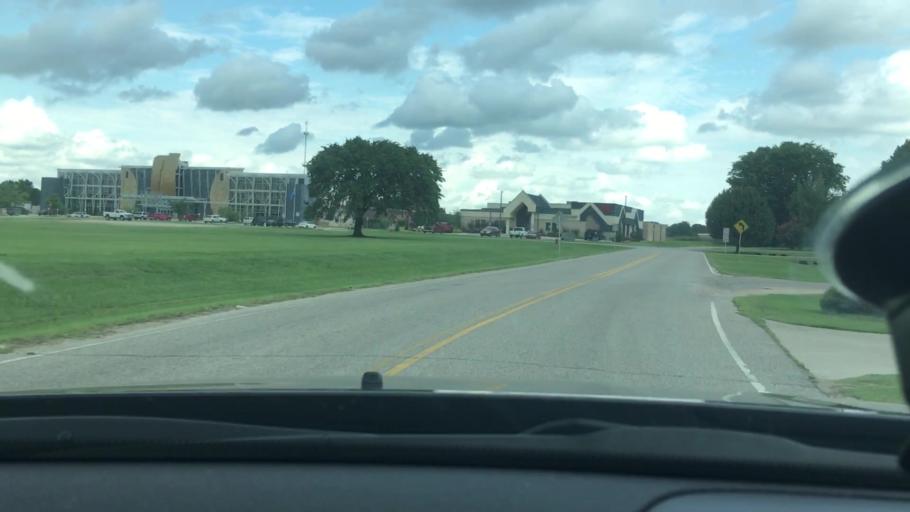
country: US
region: Oklahoma
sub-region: Johnston County
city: Tishomingo
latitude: 34.2323
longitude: -96.6626
